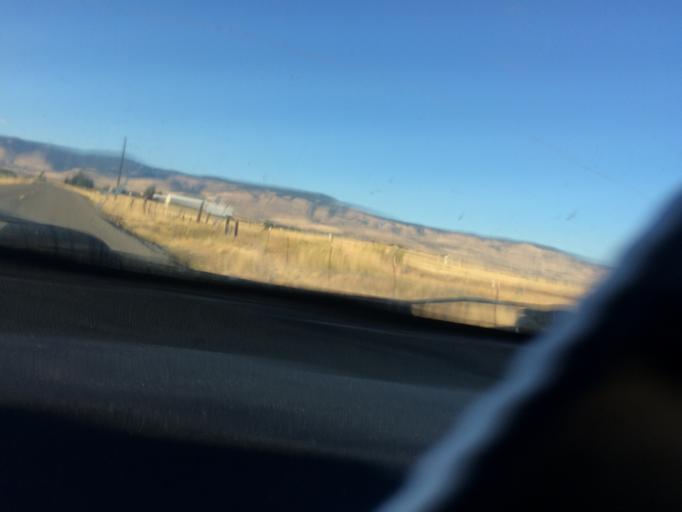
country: US
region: Washington
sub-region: Kittitas County
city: Ellensburg
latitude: 47.0866
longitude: -120.6031
